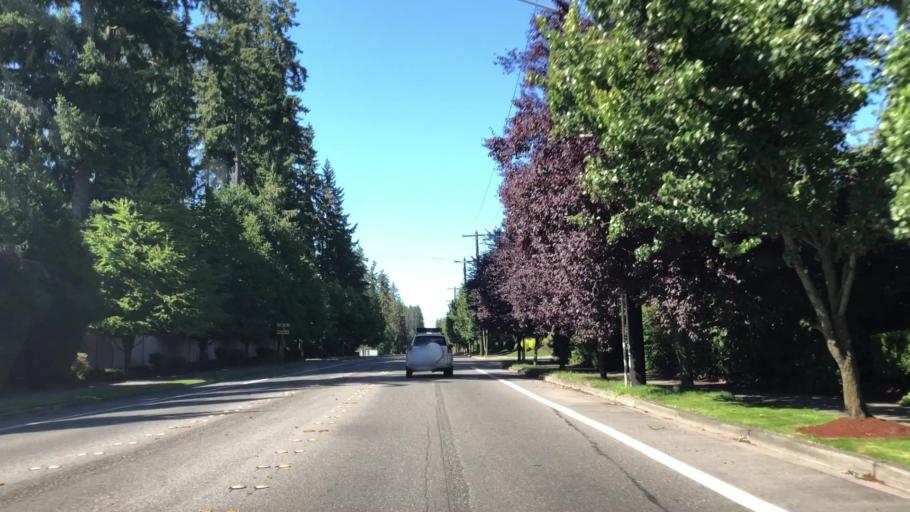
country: US
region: Washington
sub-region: Snohomish County
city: North Creek
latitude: 47.8278
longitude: -122.1859
